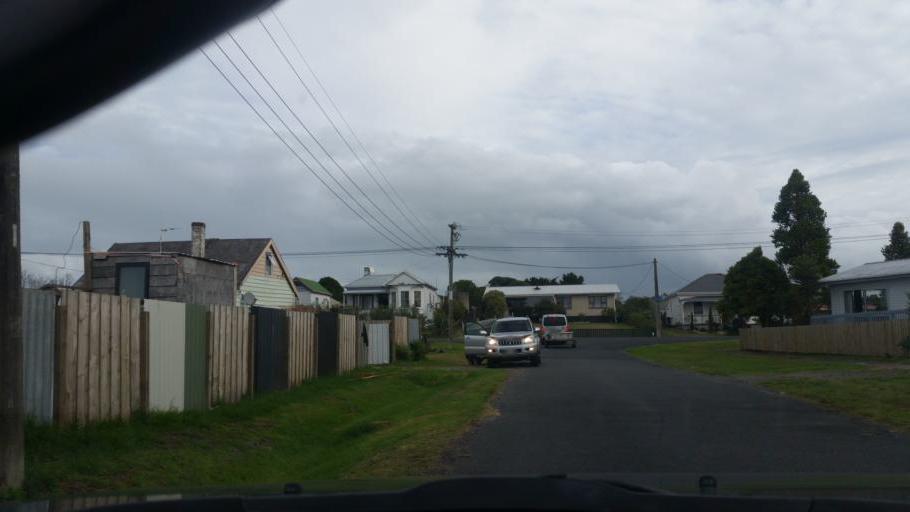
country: NZ
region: Northland
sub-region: Kaipara District
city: Dargaville
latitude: -36.0280
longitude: 173.9207
